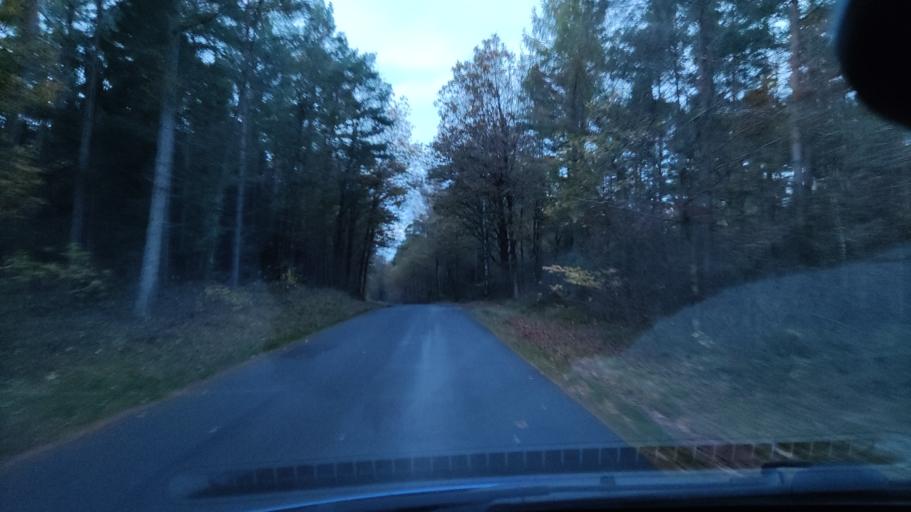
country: DE
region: Lower Saxony
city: Egestorf
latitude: 53.1566
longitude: 10.0348
